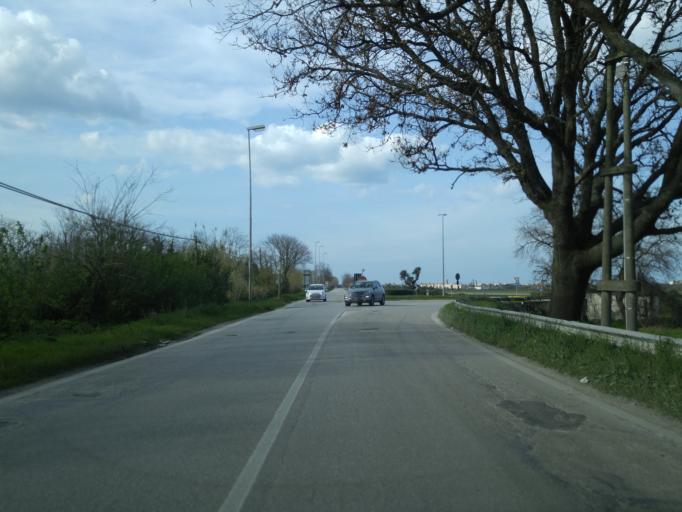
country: IT
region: The Marches
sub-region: Provincia di Pesaro e Urbino
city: Rosciano
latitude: 43.8175
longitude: 13.0175
